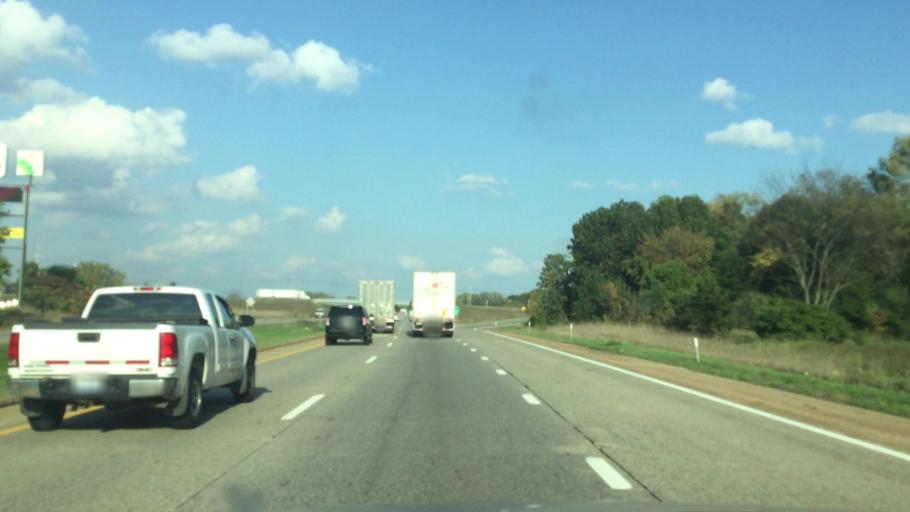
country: US
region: Michigan
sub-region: Jackson County
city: Concord
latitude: 42.2641
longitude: -84.6243
